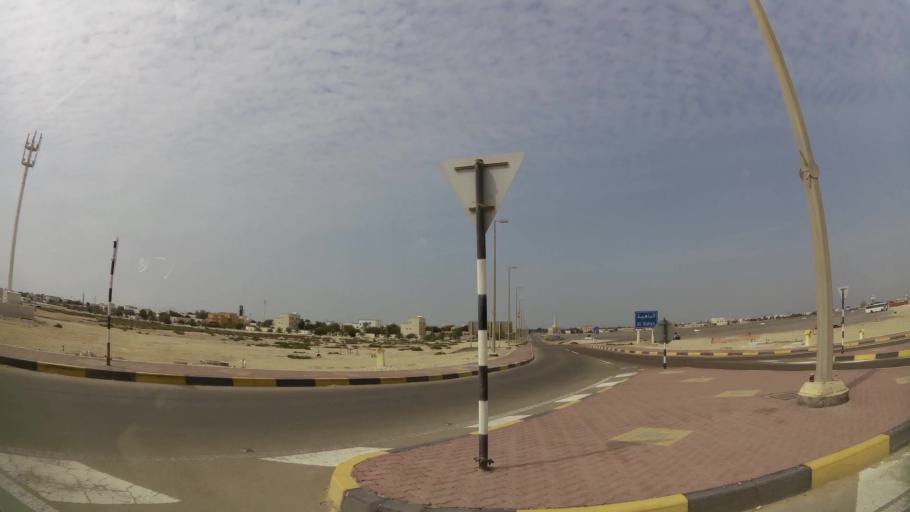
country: AE
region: Abu Dhabi
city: Abu Dhabi
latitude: 24.5299
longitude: 54.6770
